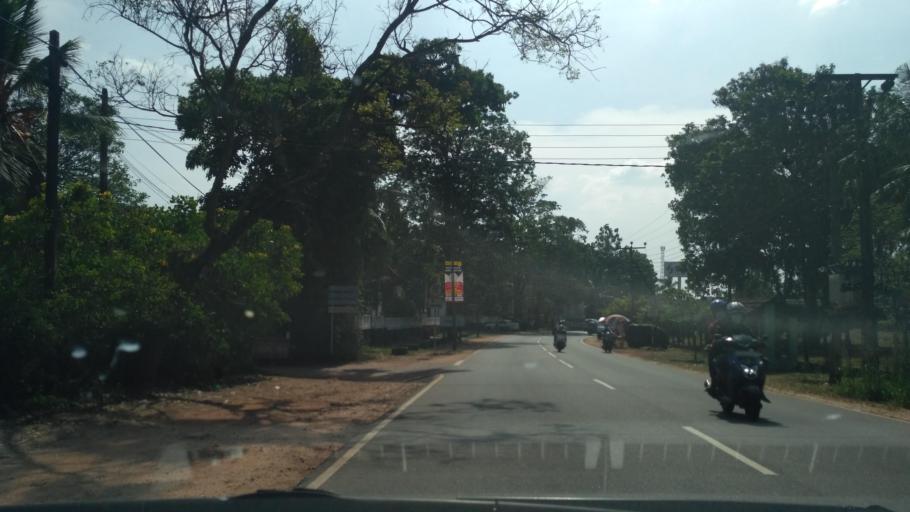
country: LK
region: North Western
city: Kuliyapitiya
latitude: 7.3331
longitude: 80.0291
